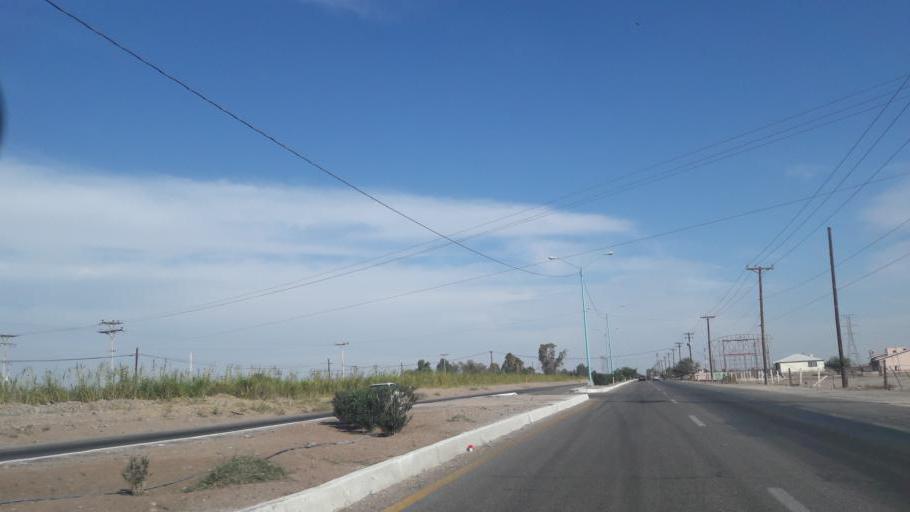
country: MX
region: Baja California
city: Progreso
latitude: 32.5858
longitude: -115.5690
